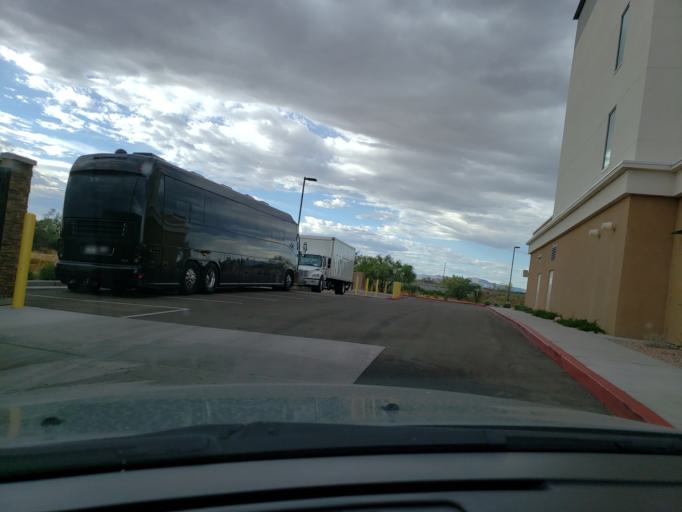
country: US
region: Arizona
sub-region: Maricopa County
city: Paradise Valley
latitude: 33.6737
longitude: -111.9833
